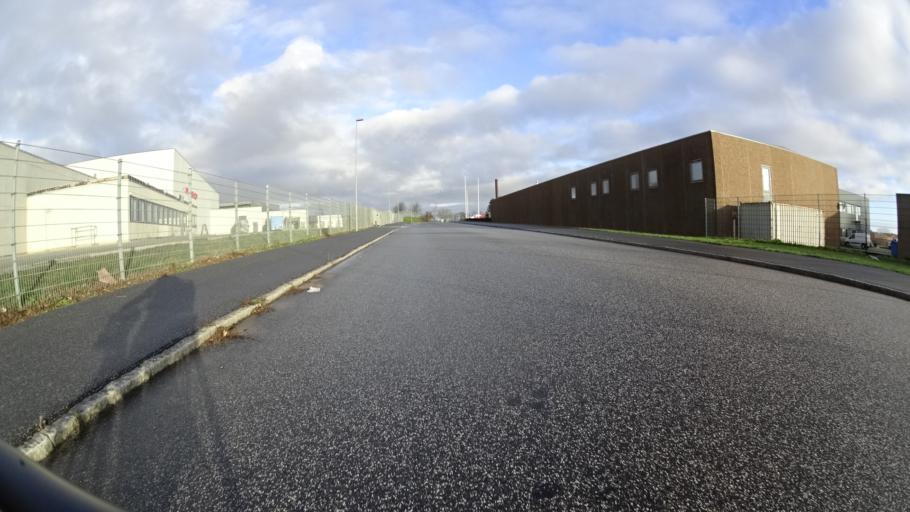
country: DK
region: Central Jutland
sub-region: Arhus Kommune
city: Tranbjerg
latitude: 56.1033
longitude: 10.1527
